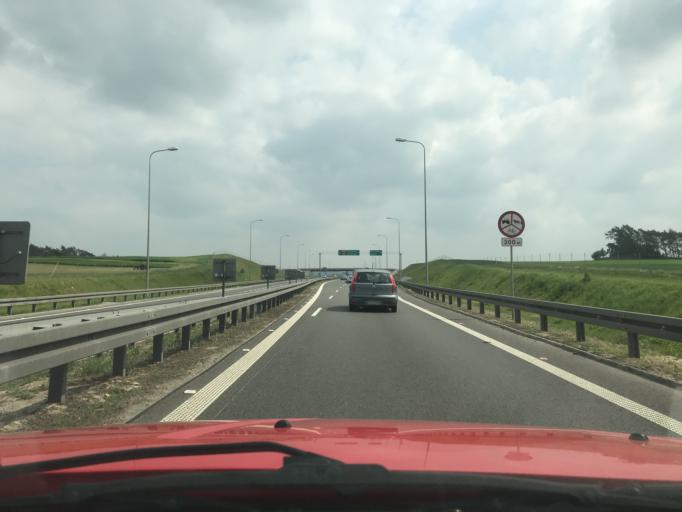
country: PL
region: Greater Poland Voivodeship
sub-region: Powiat sredzki
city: Nowe Miasto nad Warta
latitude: 52.0396
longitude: 17.4633
